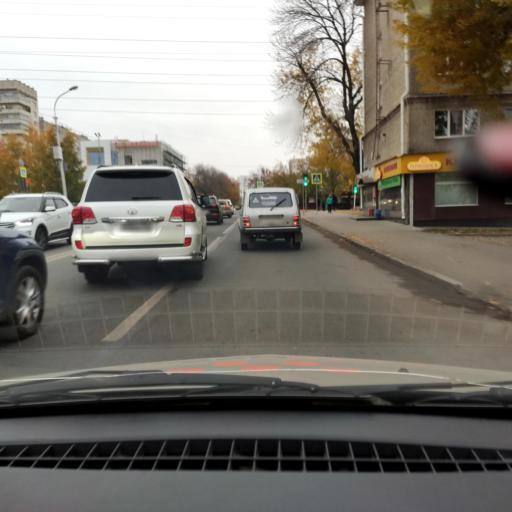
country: RU
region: Bashkortostan
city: Ufa
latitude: 54.7593
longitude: 56.0136
